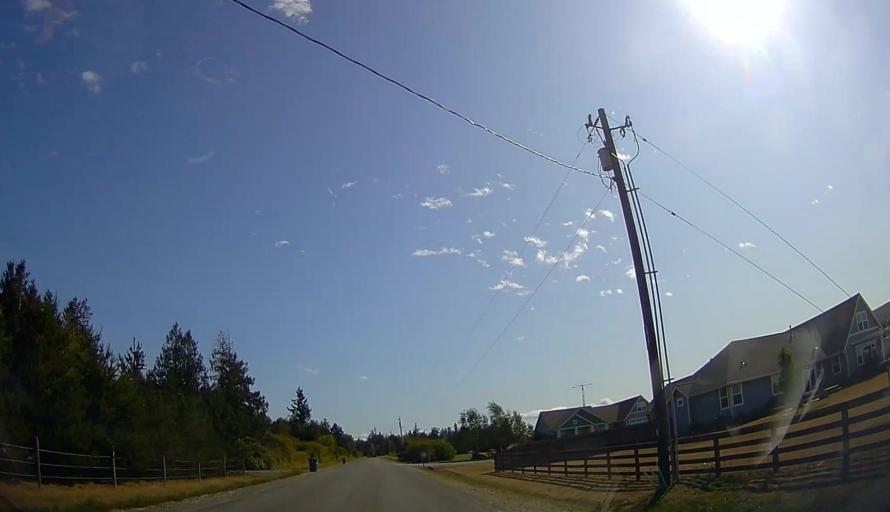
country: US
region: Washington
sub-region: Skagit County
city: Burlington
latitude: 48.4979
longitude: -122.4610
